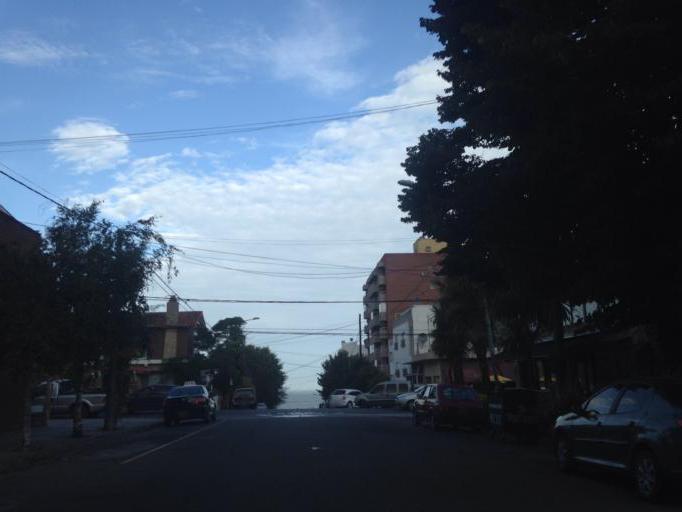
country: AR
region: Buenos Aires
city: Mar del Plata
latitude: -38.0249
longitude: -57.5343
